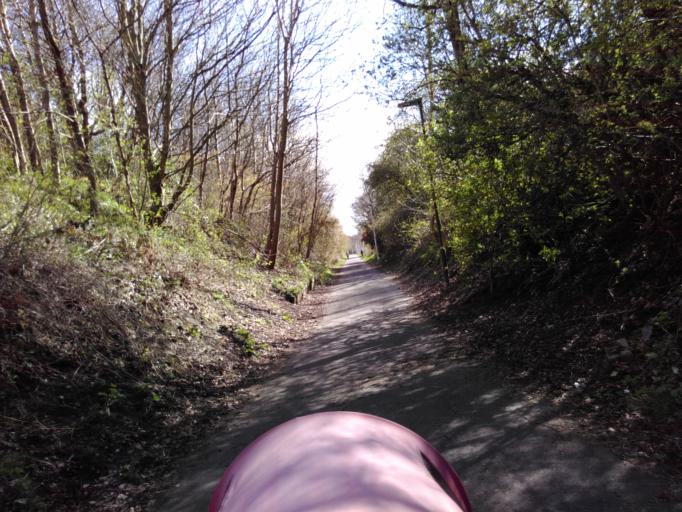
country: GB
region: Scotland
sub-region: Midlothian
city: Loanhead
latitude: 55.8756
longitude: -3.1499
